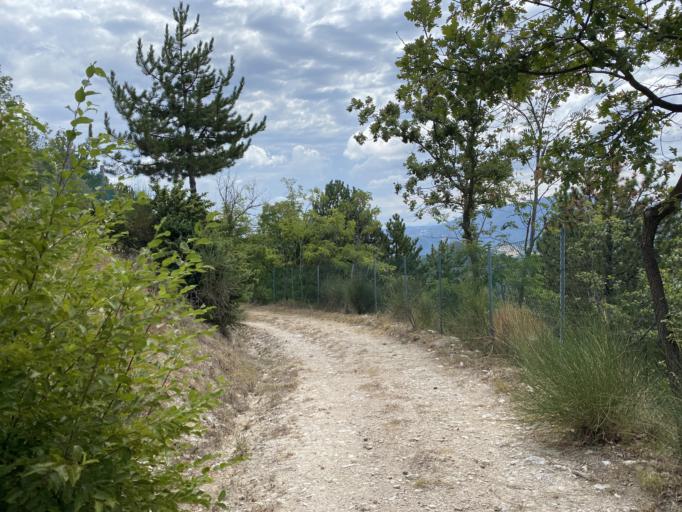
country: IT
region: The Marches
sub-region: Provincia di Pesaro e Urbino
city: Canavaccio
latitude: 43.7113
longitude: 12.7111
